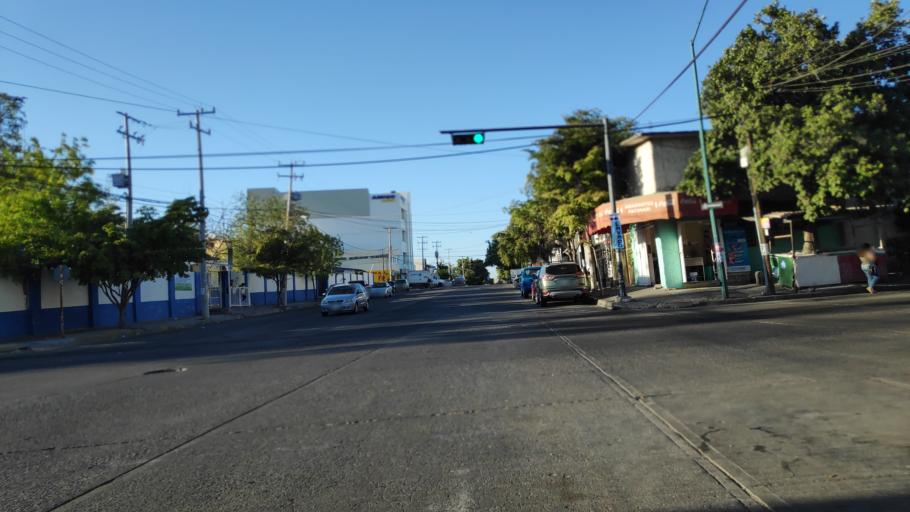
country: MX
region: Sinaloa
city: Culiacan
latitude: 24.8004
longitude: -107.4041
